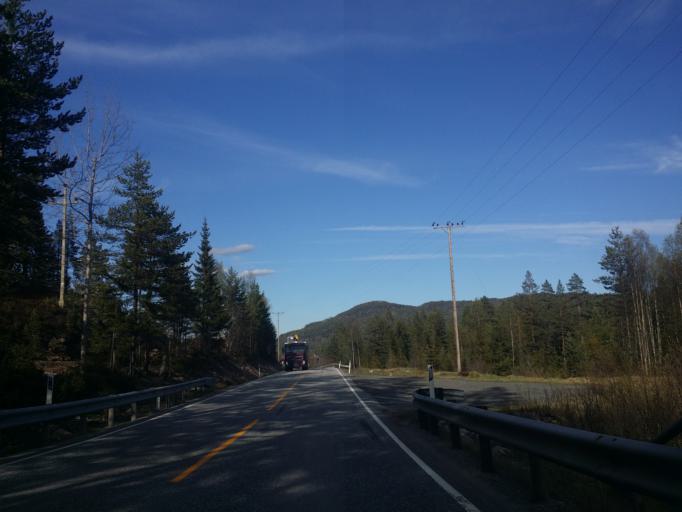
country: NO
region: Telemark
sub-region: Notodden
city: Notodden
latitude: 59.6082
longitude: 9.4447
